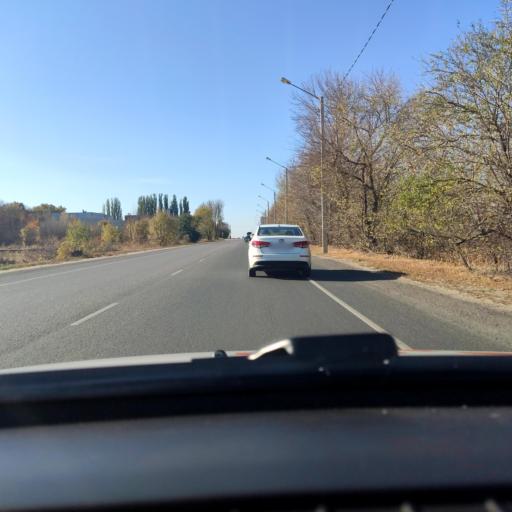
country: RU
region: Voronezj
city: Shilovo
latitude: 51.5742
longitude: 39.1431
